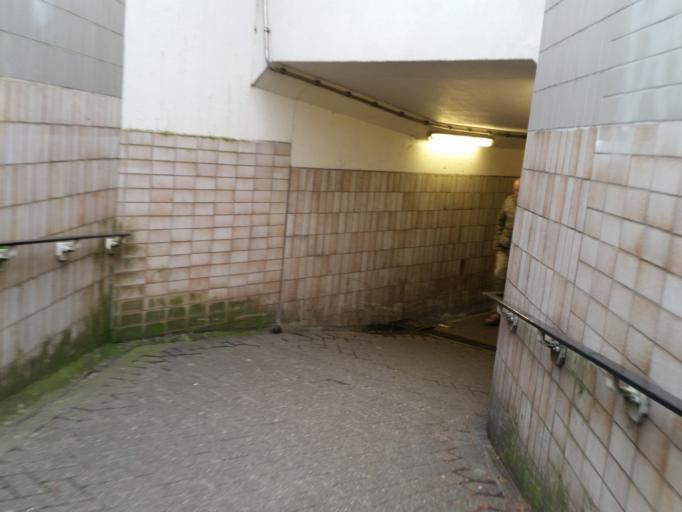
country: BE
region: Flanders
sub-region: Provincie Antwerpen
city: Lier
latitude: 51.1362
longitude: 4.5625
